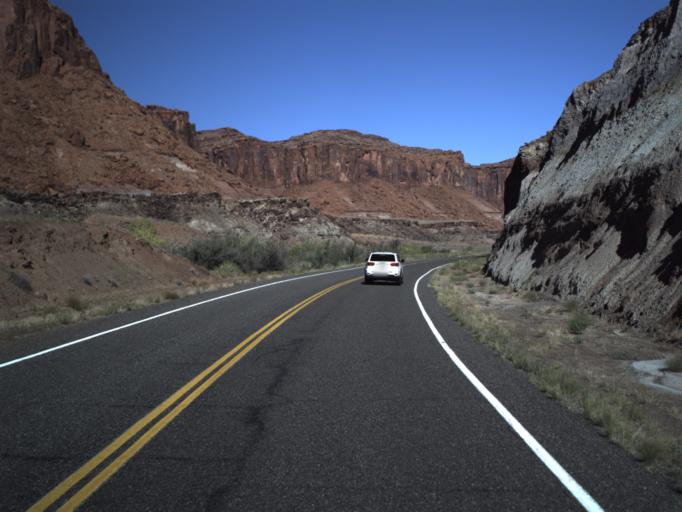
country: US
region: Utah
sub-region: San Juan County
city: Blanding
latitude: 37.9066
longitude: -110.4559
